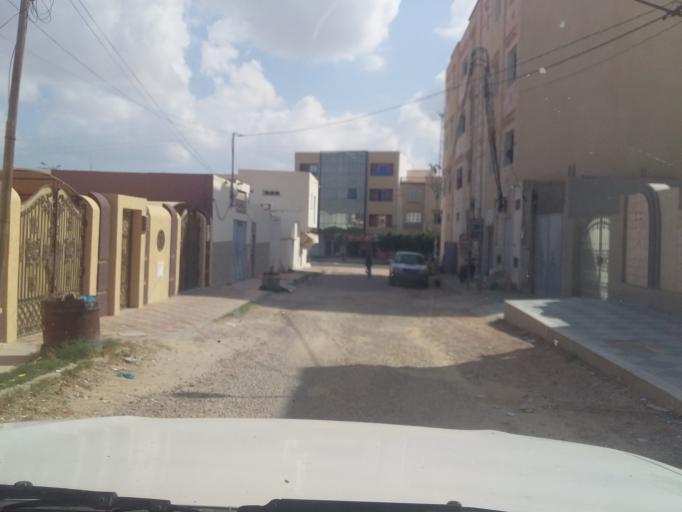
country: TN
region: Qabis
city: Gabes
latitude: 33.6242
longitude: 10.2814
